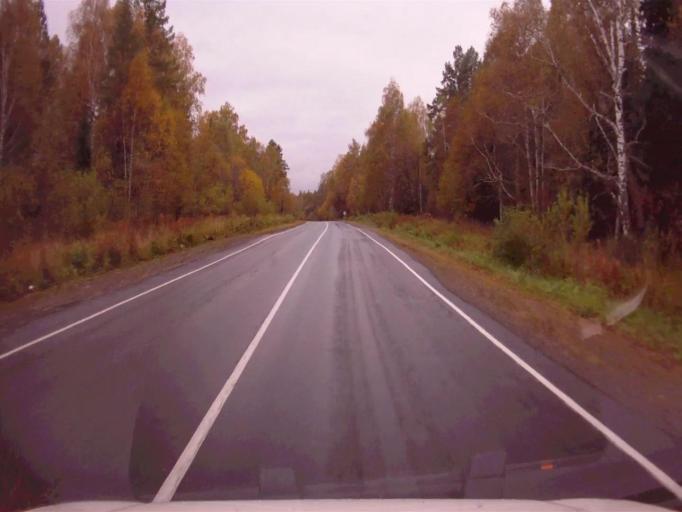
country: RU
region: Chelyabinsk
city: Nizhniy Ufaley
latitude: 56.0658
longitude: 60.0034
